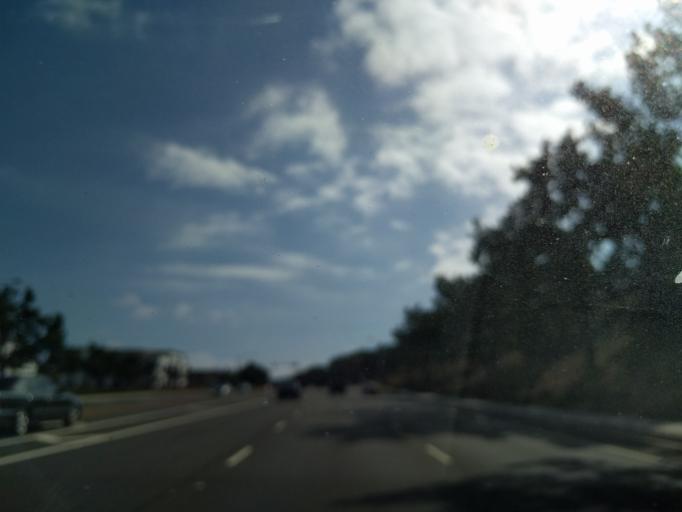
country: US
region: California
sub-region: Orange County
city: Aliso Viejo
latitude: 33.5657
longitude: -117.7243
